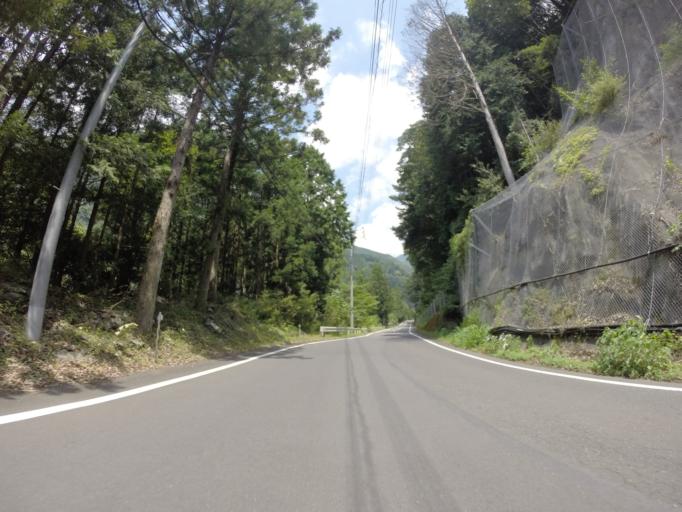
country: JP
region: Shizuoka
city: Fujinomiya
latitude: 35.2683
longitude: 138.3266
